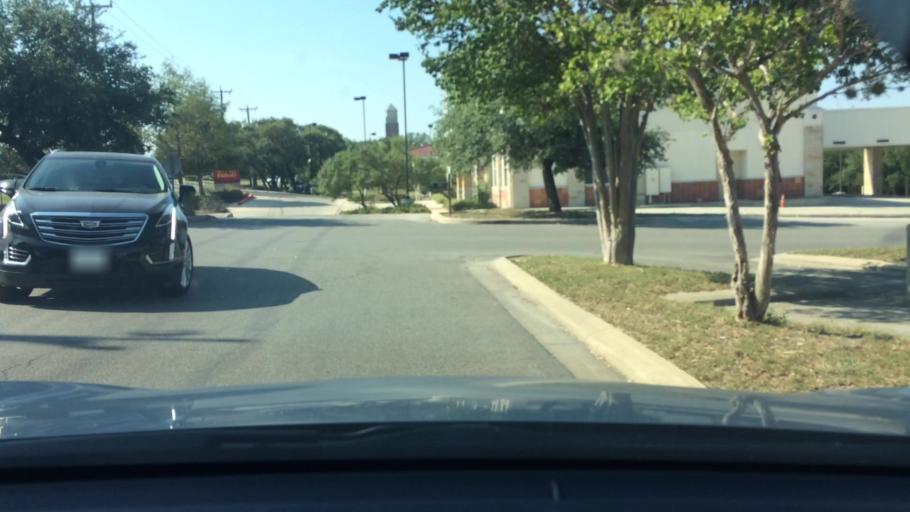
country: US
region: Texas
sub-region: Bexar County
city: Hollywood Park
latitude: 29.6119
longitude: -98.5084
